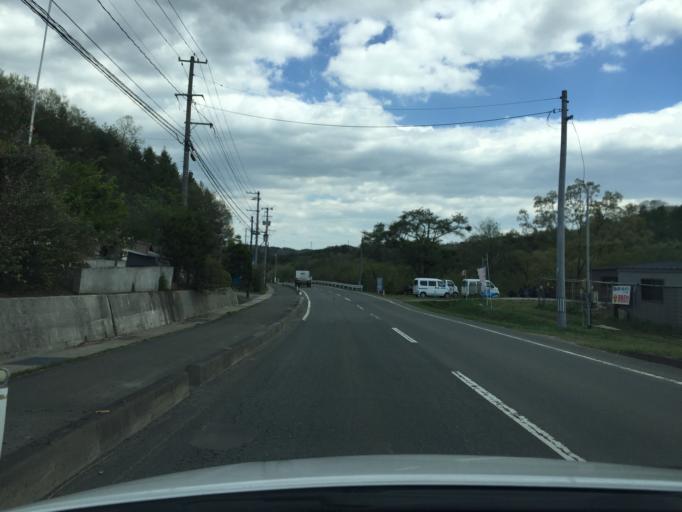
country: JP
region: Fukushima
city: Yanagawamachi-saiwaicho
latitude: 37.6826
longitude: 140.7390
